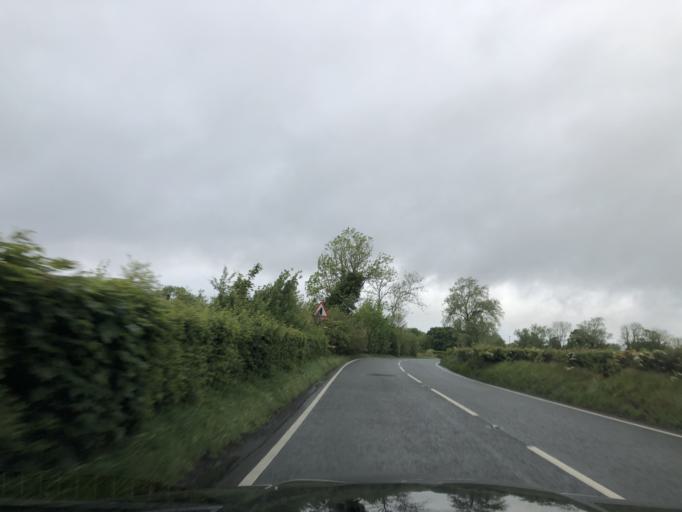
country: GB
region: Northern Ireland
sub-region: Antrim Borough
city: Antrim
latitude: 54.6786
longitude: -6.2228
